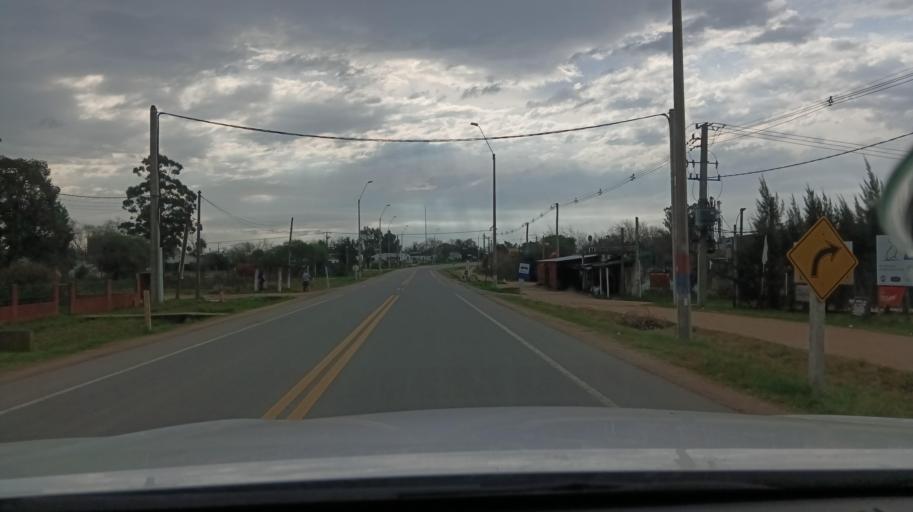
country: UY
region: Canelones
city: Toledo
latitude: -34.7374
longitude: -56.1137
